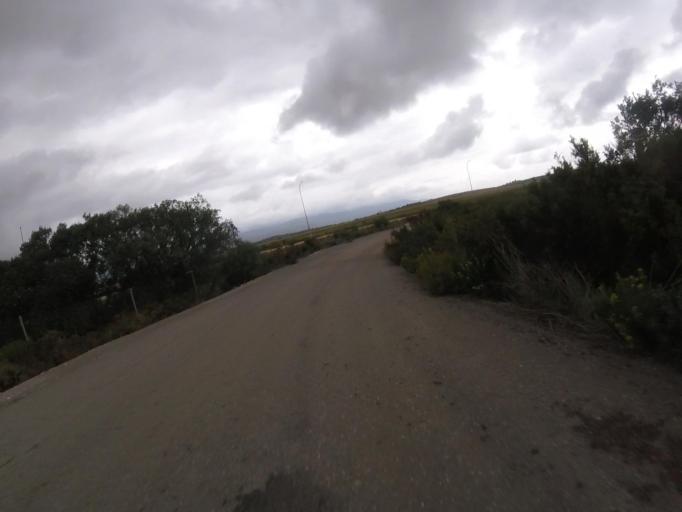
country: ES
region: Valencia
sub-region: Provincia de Castello
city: Benlloch
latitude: 40.2101
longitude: 0.0762
